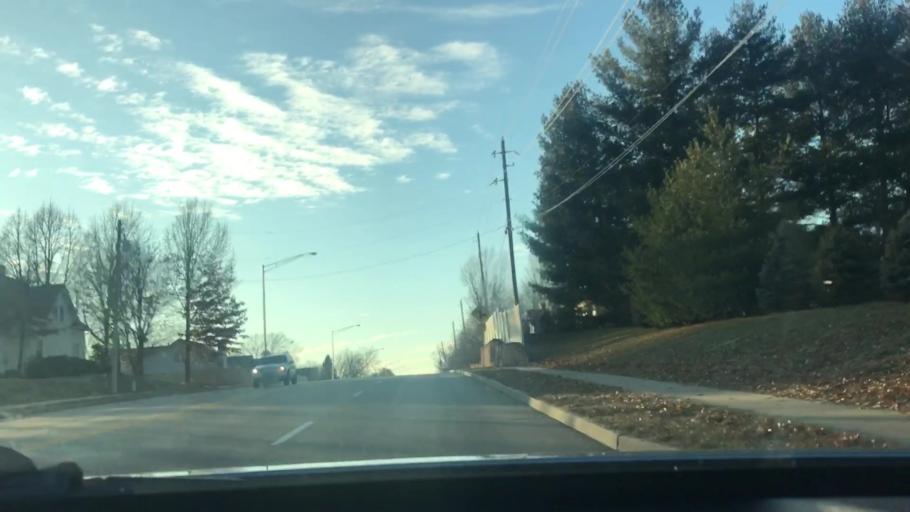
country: US
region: Missouri
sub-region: Jackson County
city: Lees Summit
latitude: 38.9315
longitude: -94.3511
